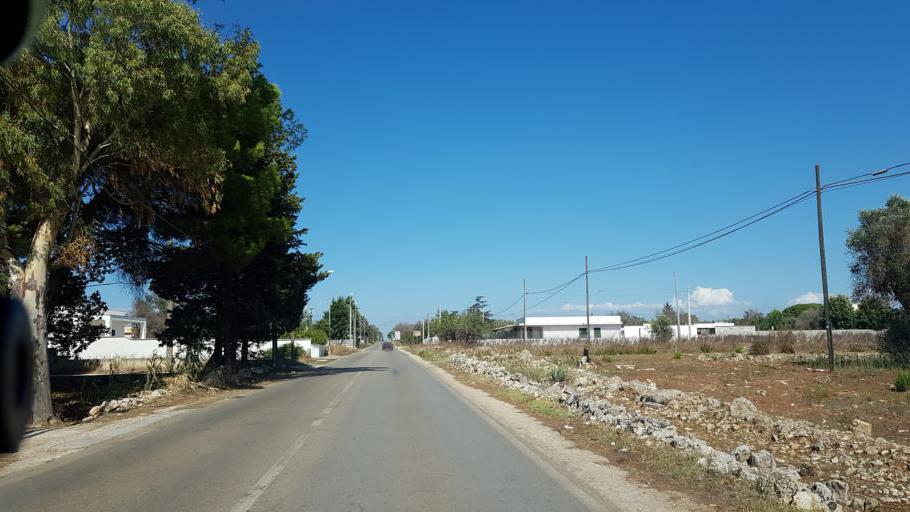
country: IT
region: Apulia
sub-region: Provincia di Lecce
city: Porto Cesareo
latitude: 40.2212
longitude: 17.9334
